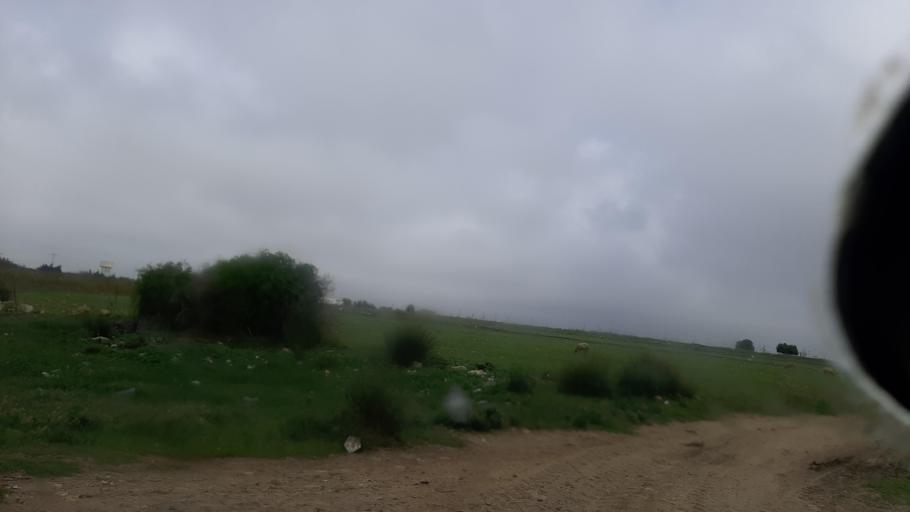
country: TN
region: Nabul
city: Qulaybiyah
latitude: 36.8322
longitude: 11.0330
